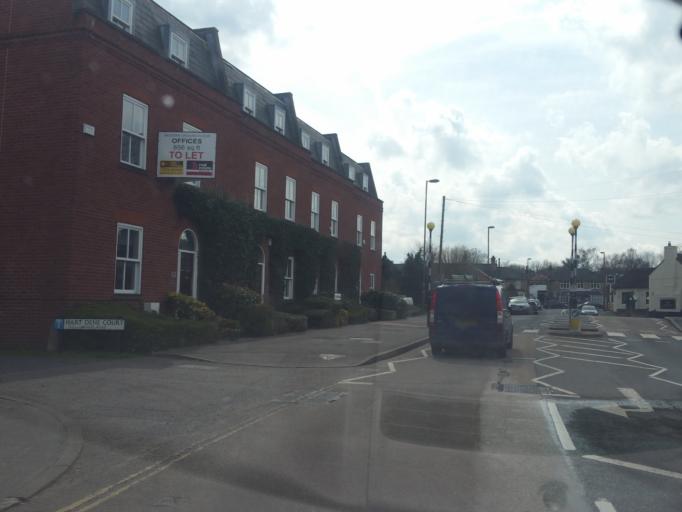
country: GB
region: England
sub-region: Surrey
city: Bagshot
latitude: 51.3630
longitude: -0.6910
